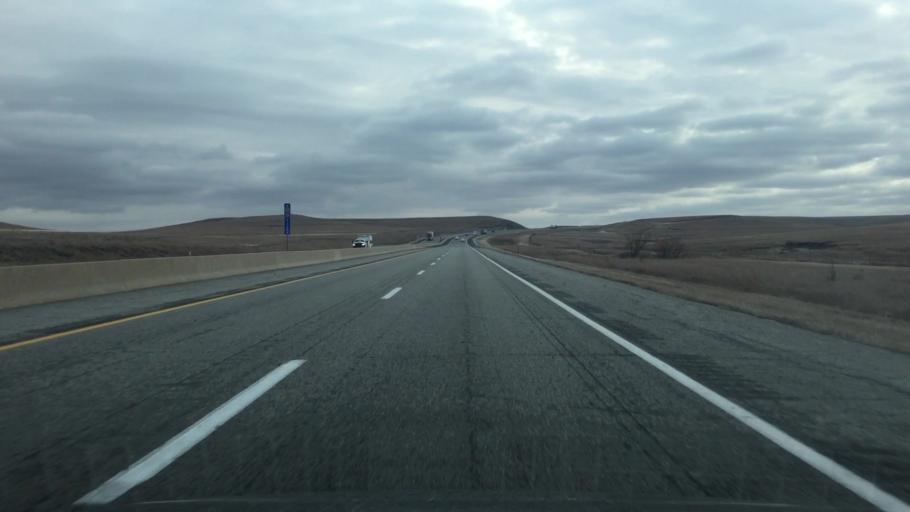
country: US
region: Kansas
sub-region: Chase County
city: Cottonwood Falls
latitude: 38.2477
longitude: -96.3938
